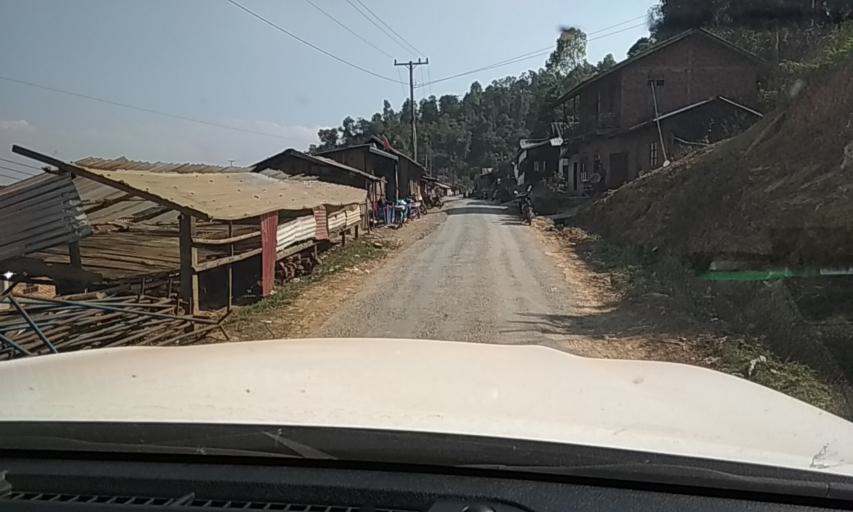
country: LA
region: Phongsali
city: Phongsali
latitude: 21.6632
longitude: 102.0896
